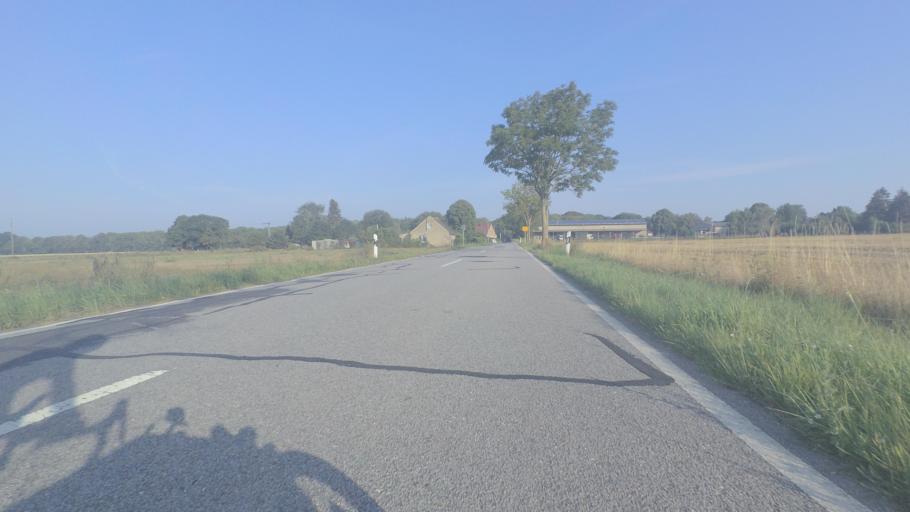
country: DE
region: Mecklenburg-Vorpommern
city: Demmin
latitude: 53.9519
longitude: 13.1138
